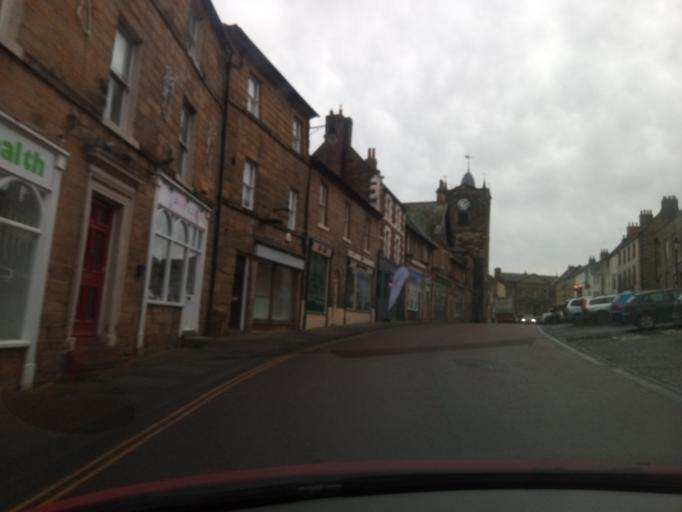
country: GB
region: England
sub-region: Northumberland
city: Alnwick
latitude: 55.4142
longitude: -1.7078
